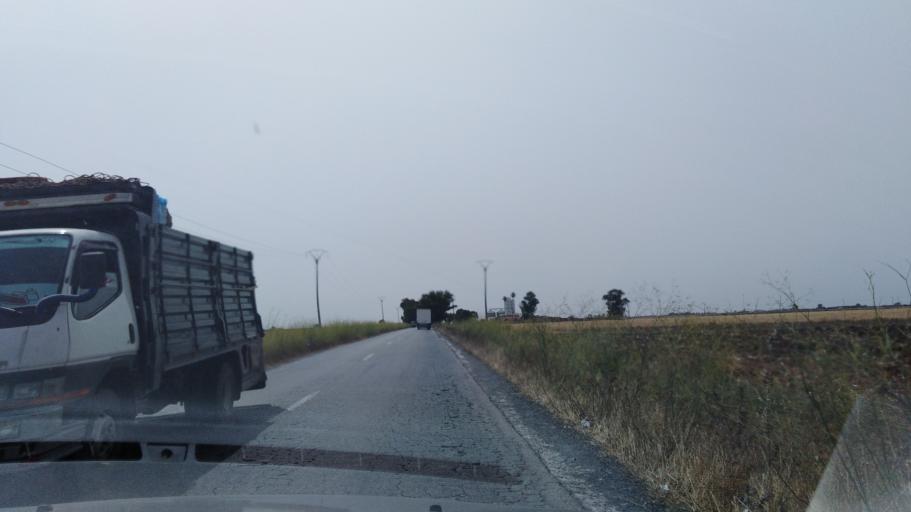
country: MA
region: Grand Casablanca
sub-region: Nouaceur
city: Dar Bouazza
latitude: 33.3991
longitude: -7.8028
